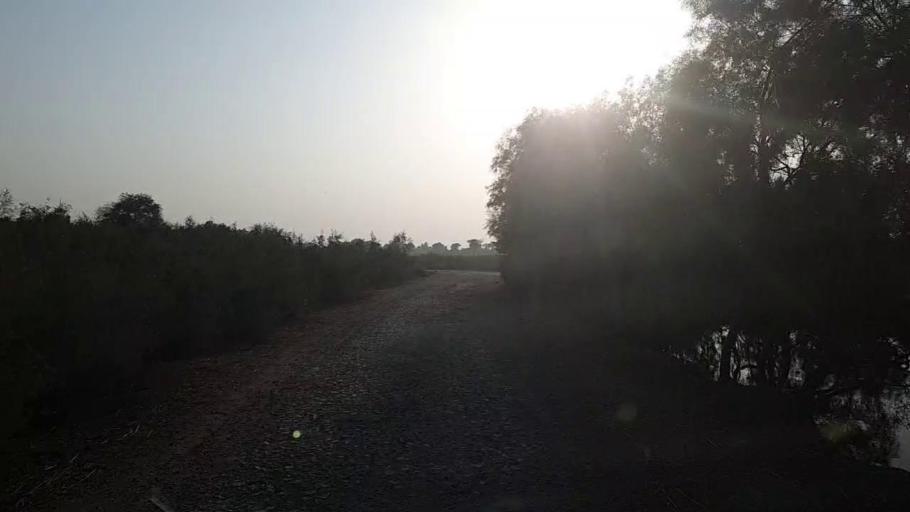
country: PK
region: Sindh
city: Kandhkot
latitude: 28.2384
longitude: 69.0924
